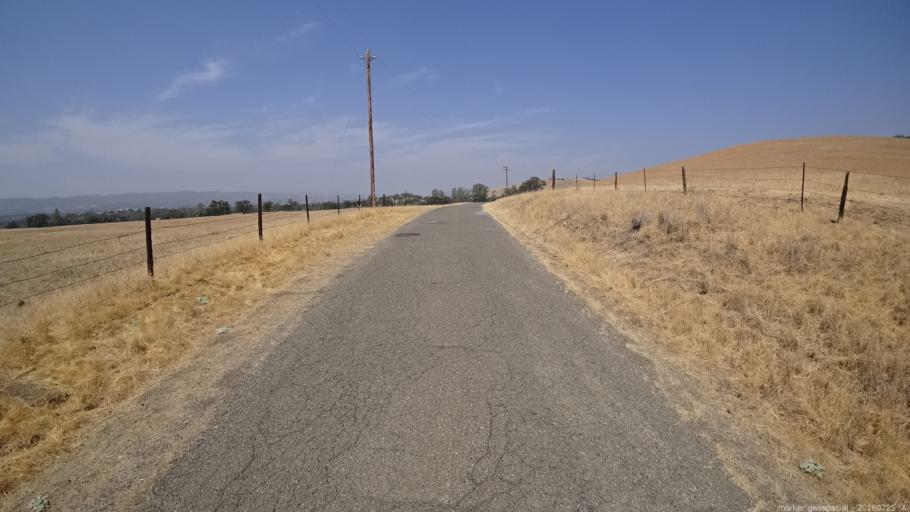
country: US
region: California
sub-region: San Luis Obispo County
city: Shandon
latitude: 35.8772
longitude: -120.3920
